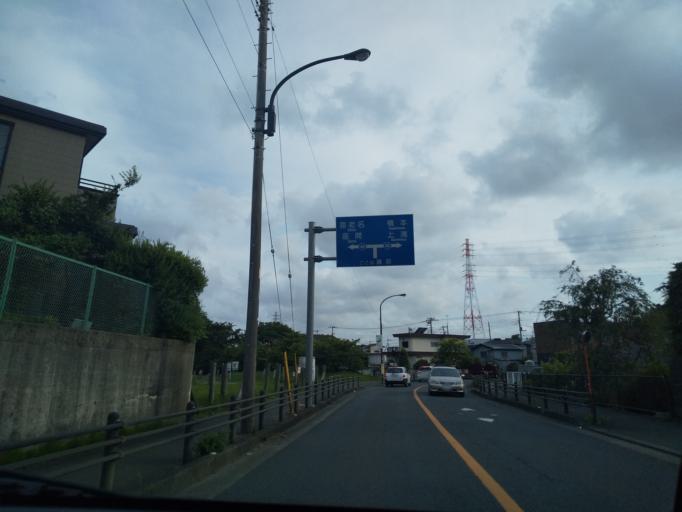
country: JP
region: Kanagawa
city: Zama
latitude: 35.5112
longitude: 139.3862
